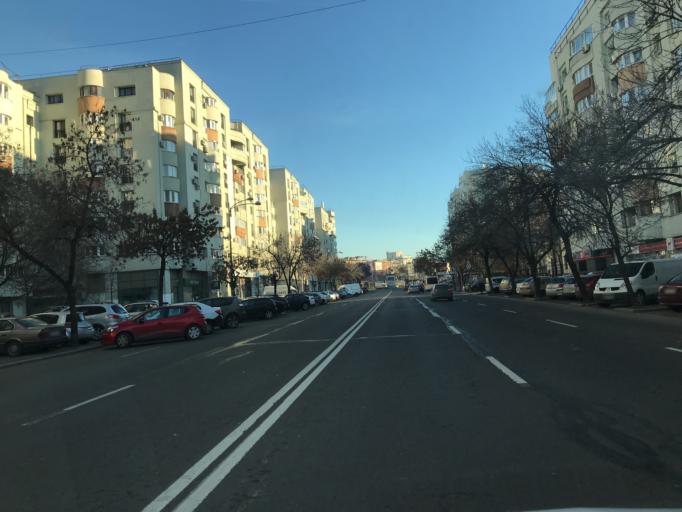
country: RO
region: Bucuresti
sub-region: Municipiul Bucuresti
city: Bucuresti
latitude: 44.4388
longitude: 26.0791
